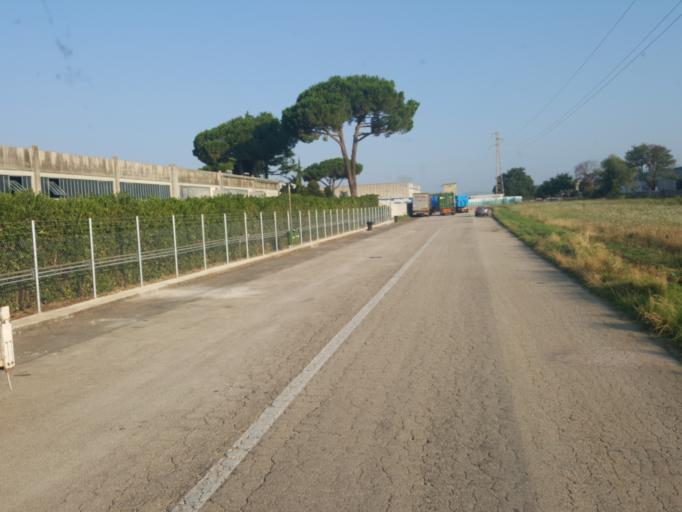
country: IT
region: Latium
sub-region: Provincia di Latina
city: Borgo Podgora
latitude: 41.5551
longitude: 12.8628
